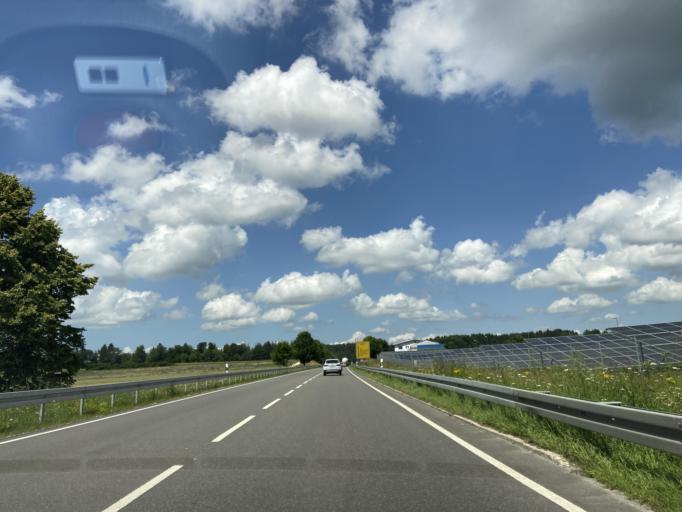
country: DE
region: Baden-Wuerttemberg
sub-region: Tuebingen Region
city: Strassberg
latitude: 48.1782
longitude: 9.1040
